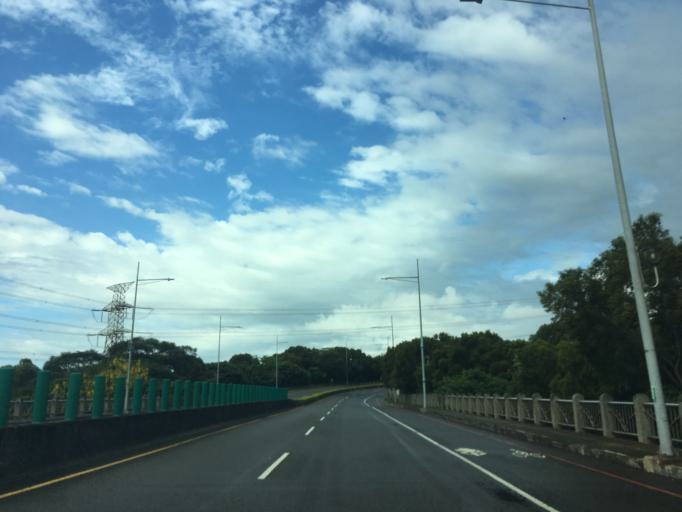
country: TW
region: Taiwan
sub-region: Taichung City
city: Taichung
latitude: 24.1999
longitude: 120.6031
